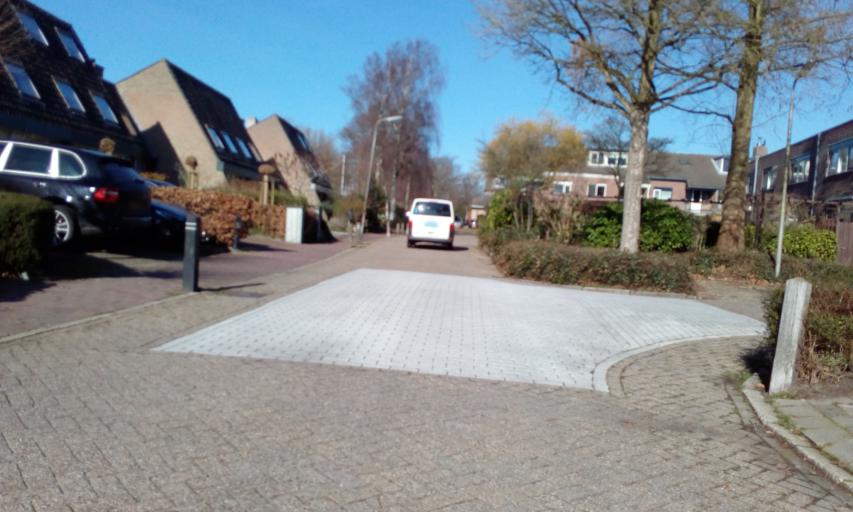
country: NL
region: South Holland
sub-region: Gemeente Lansingerland
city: Bleiswijk
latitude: 52.0072
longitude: 4.5782
